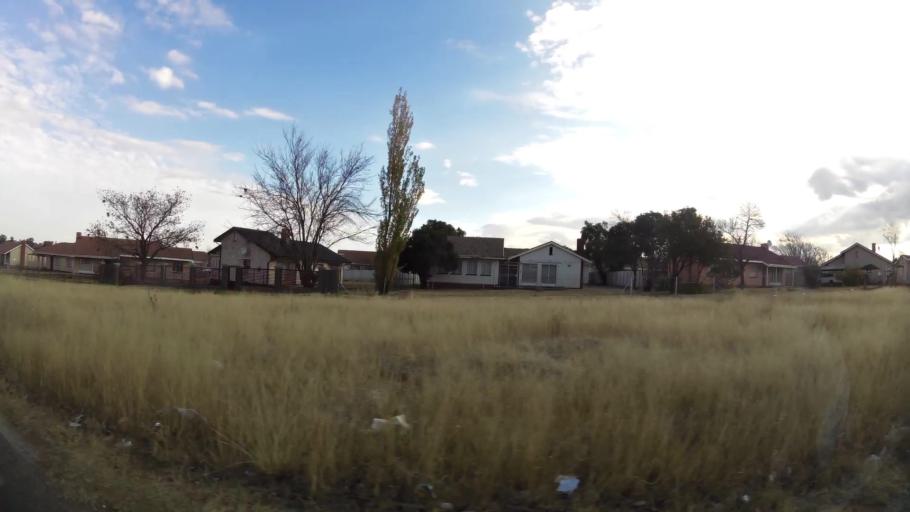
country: ZA
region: Orange Free State
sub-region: Lejweleputswa District Municipality
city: Welkom
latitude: -27.9837
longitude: 26.7025
